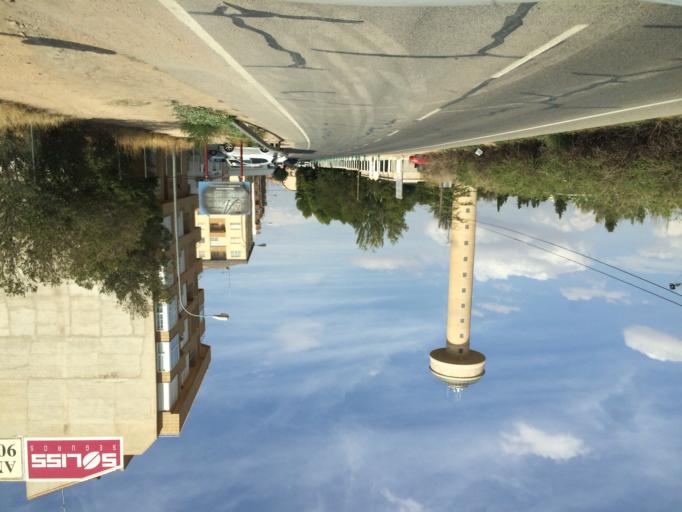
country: ES
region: Castille-La Mancha
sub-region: Provincia de Albacete
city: Albacete
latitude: 38.9981
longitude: -1.8773
